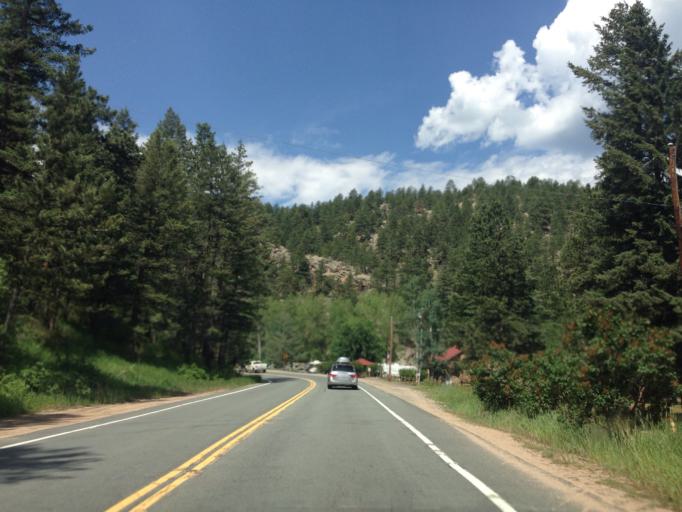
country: US
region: Colorado
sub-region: Larimer County
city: Estes Park
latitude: 40.4084
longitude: -105.4117
